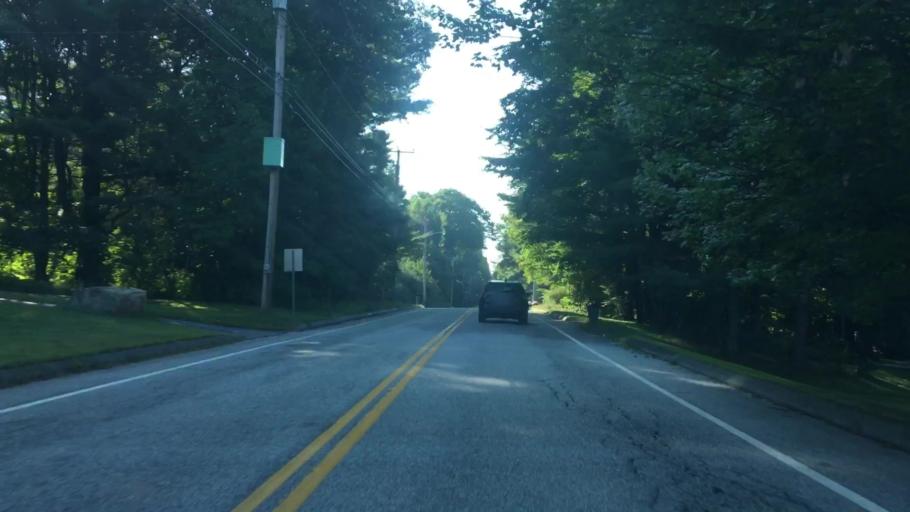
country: US
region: Maine
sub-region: Androscoggin County
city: Minot
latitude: 44.0457
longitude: -70.2707
